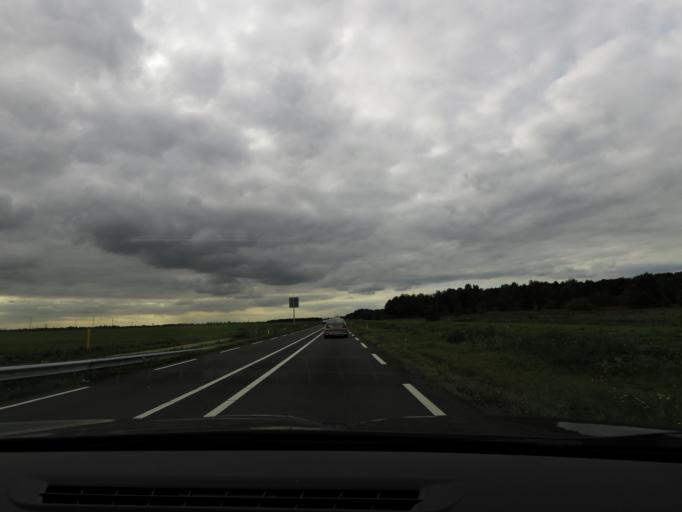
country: NL
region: South Holland
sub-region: Molenwaard
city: Nieuw-Lekkerland
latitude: 51.9277
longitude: 4.7125
